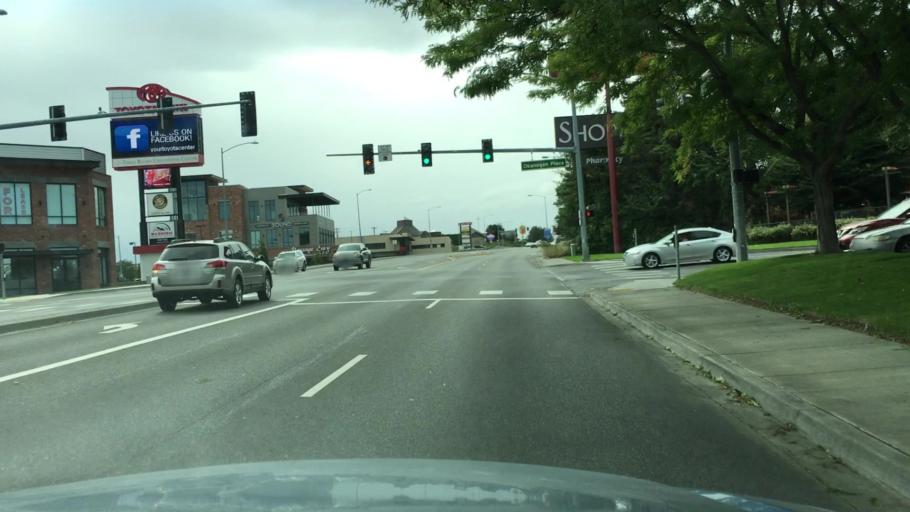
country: US
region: Washington
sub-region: Franklin County
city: West Pasco
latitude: 46.2212
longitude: -119.2241
